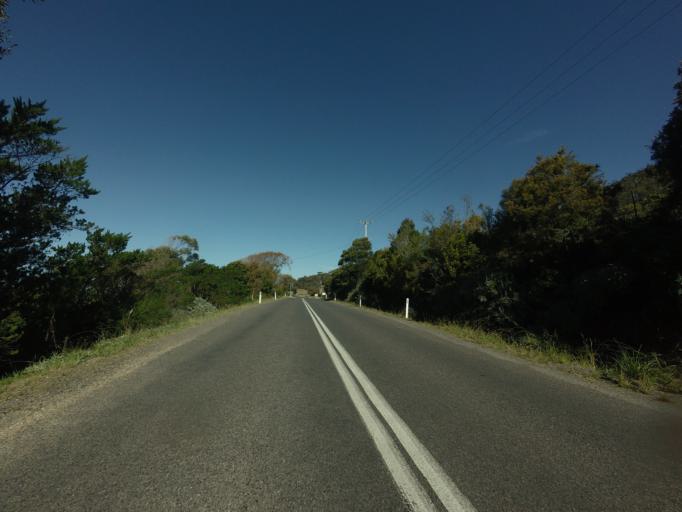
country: AU
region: Tasmania
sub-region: Break O'Day
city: St Helens
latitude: -41.8581
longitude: 148.2752
